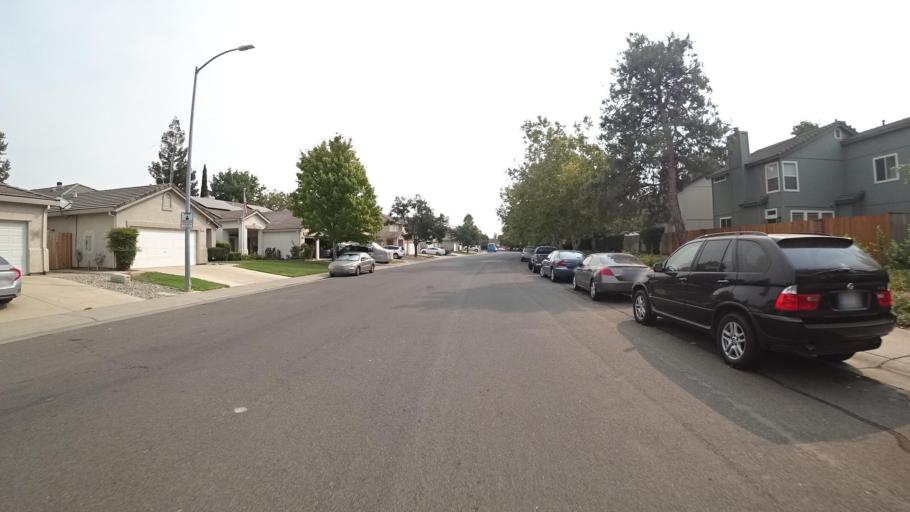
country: US
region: California
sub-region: Sacramento County
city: Laguna
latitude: 38.4120
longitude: -121.4041
